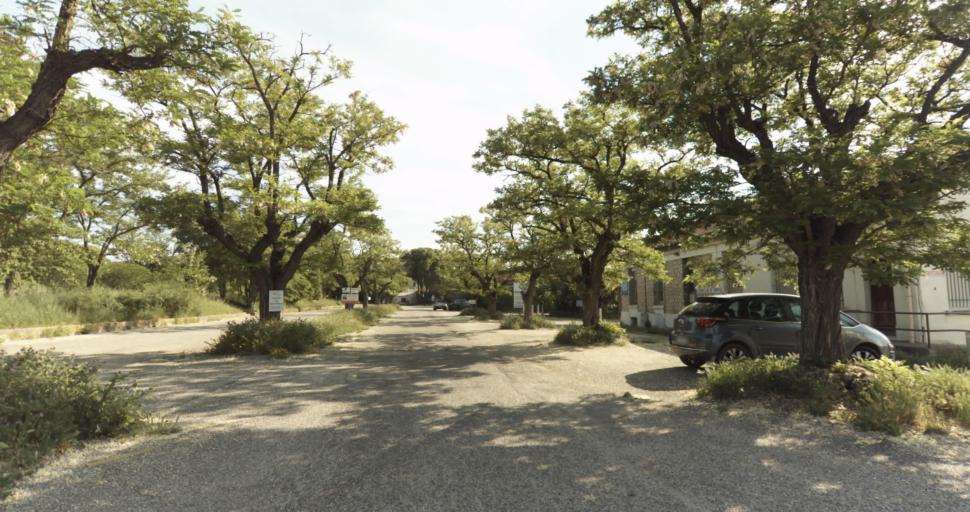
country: FR
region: Languedoc-Roussillon
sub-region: Departement du Gard
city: Marguerittes
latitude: 43.8574
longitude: 4.4068
